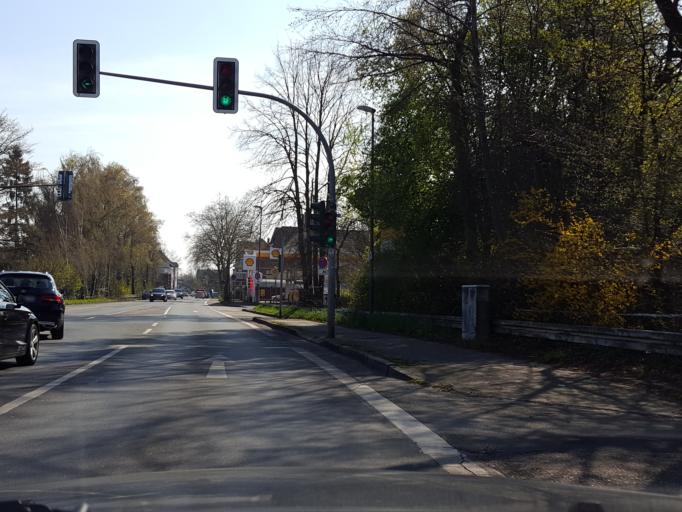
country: DE
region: North Rhine-Westphalia
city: Castrop-Rauxel
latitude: 51.6027
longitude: 7.3144
